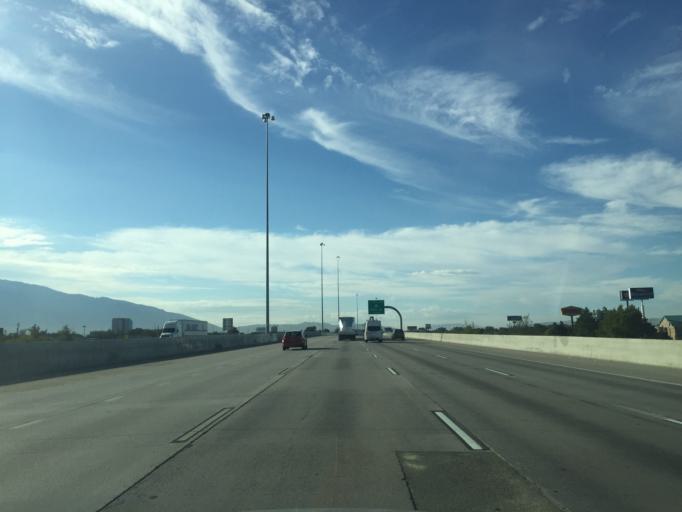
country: US
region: Utah
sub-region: Salt Lake County
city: Centerfield
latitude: 40.6772
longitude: -111.9020
